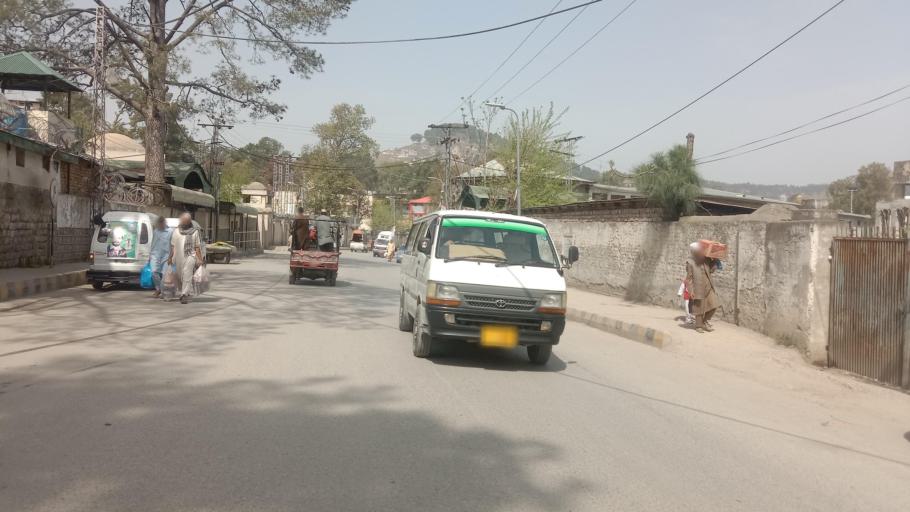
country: PK
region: Khyber Pakhtunkhwa
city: Abbottabad
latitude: 34.1419
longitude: 73.2130
